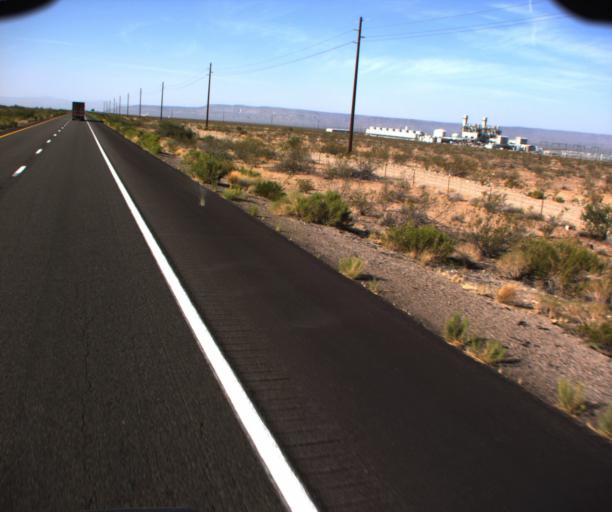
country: US
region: Arizona
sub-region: Mohave County
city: Kingman
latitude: 35.0602
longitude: -114.1258
